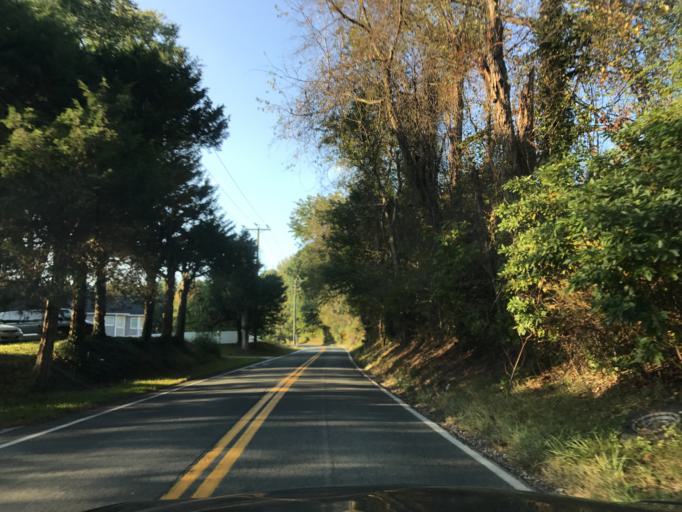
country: US
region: Maryland
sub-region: Anne Arundel County
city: Gambrills
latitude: 39.0350
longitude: -76.6535
